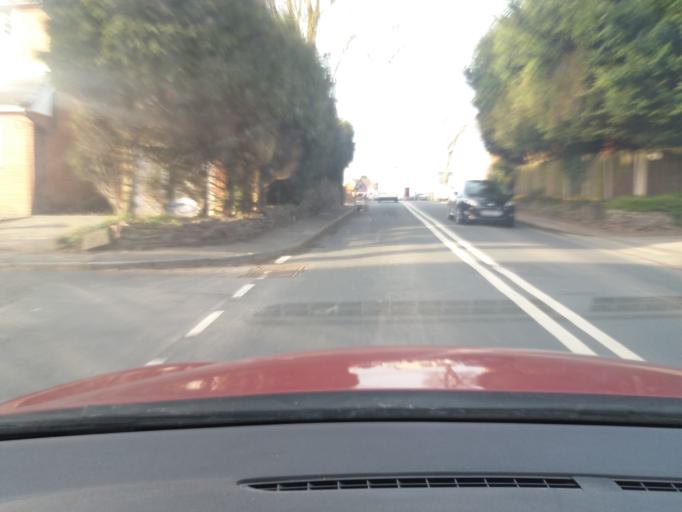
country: GB
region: England
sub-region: Lancashire
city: Euxton
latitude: 53.6575
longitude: -2.6745
